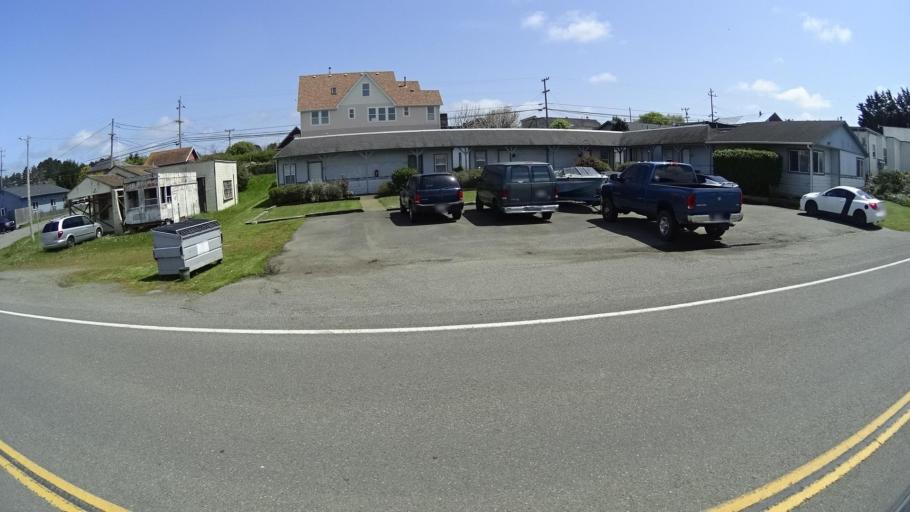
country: US
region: California
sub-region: Humboldt County
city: Ferndale
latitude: 40.6415
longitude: -124.2266
